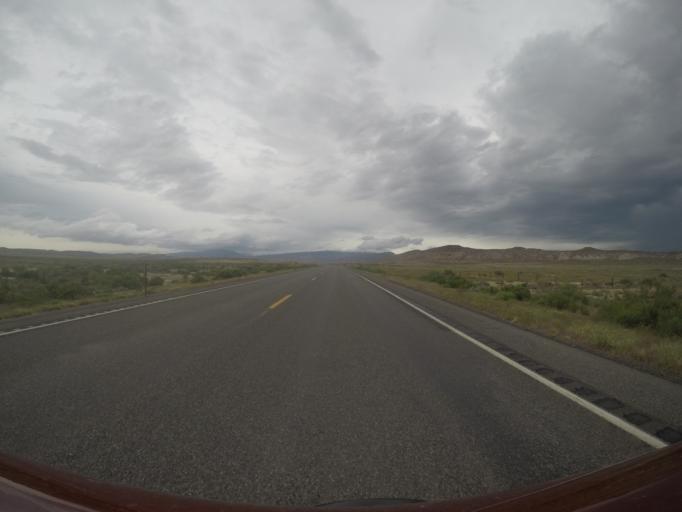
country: US
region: Wyoming
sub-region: Big Horn County
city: Lovell
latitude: 44.9110
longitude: -108.2917
